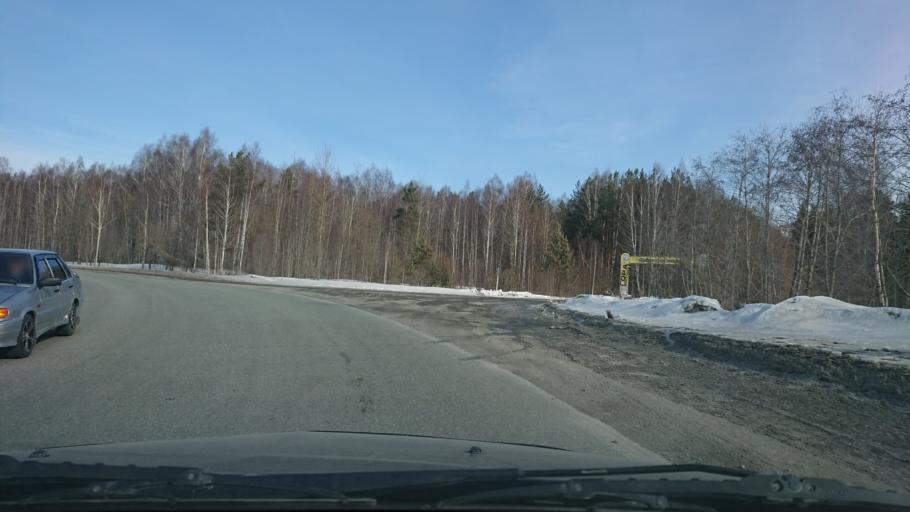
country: RU
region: Sverdlovsk
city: Revda
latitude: 56.8225
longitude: 59.9802
